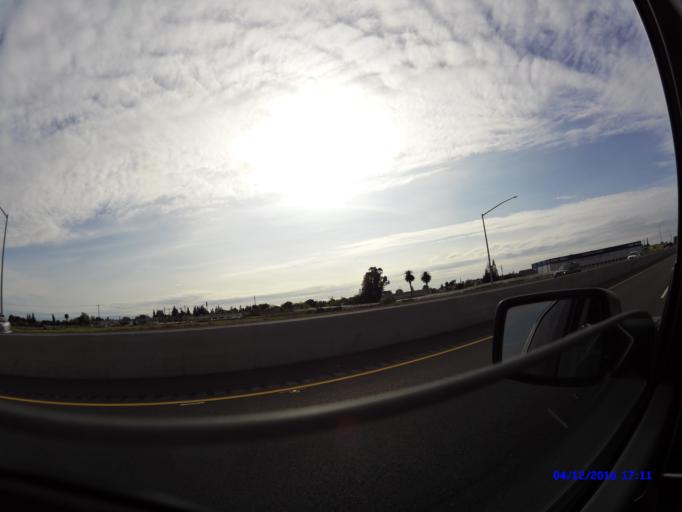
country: US
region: California
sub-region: San Joaquin County
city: Manteca
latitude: 37.8204
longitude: -121.2148
